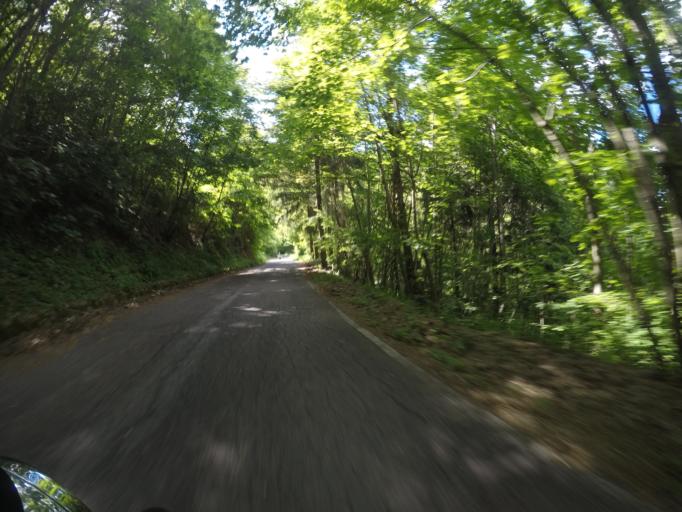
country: IT
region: Tuscany
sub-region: Provincia di Lucca
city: Minucciano
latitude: 44.1642
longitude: 10.2024
